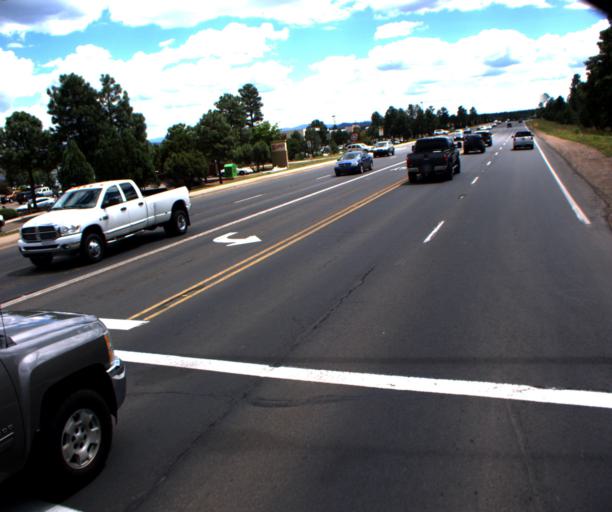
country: US
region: Arizona
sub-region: Navajo County
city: Lake of the Woods
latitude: 34.2019
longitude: -110.0192
